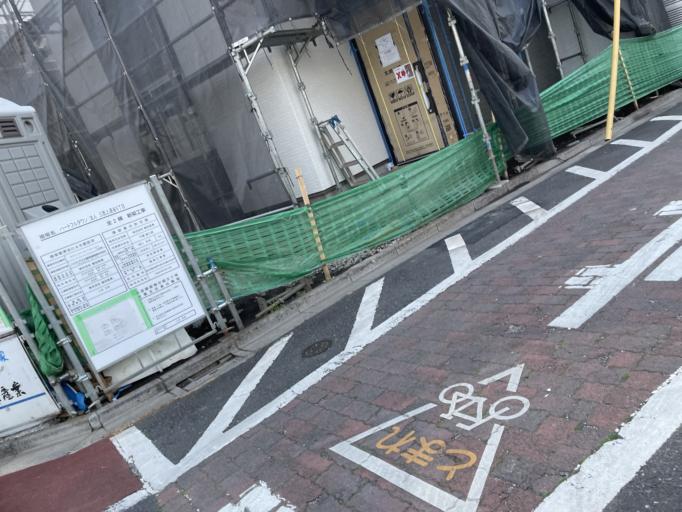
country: JP
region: Tokyo
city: Kamirenjaku
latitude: 35.6969
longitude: 139.5537
